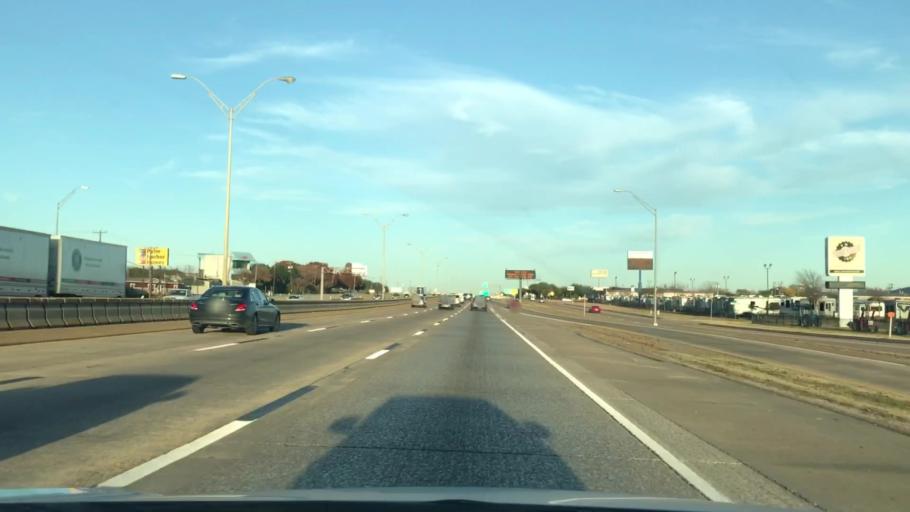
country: US
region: Texas
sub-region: Dallas County
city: Mesquite
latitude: 32.8051
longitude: -96.6655
